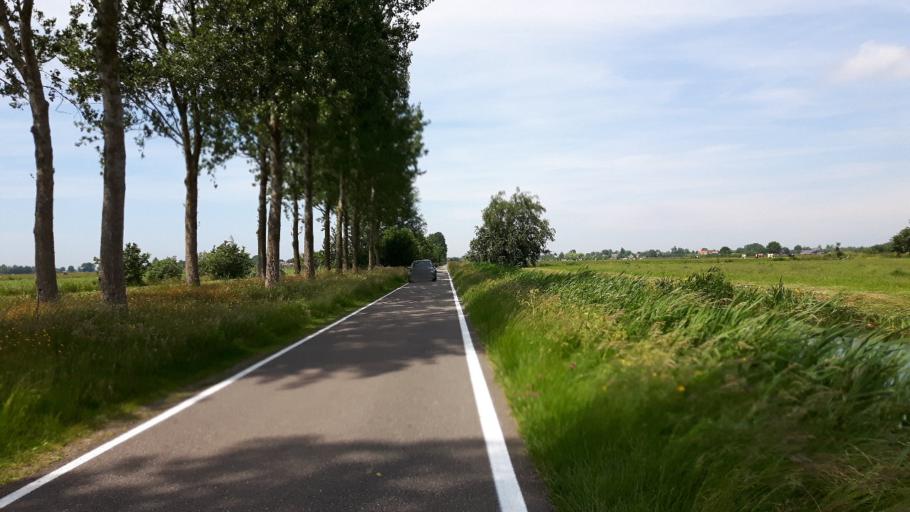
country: NL
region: South Holland
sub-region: Gemeente Nieuwkoop
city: Nieuwkoop
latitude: 52.1160
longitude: 4.8063
